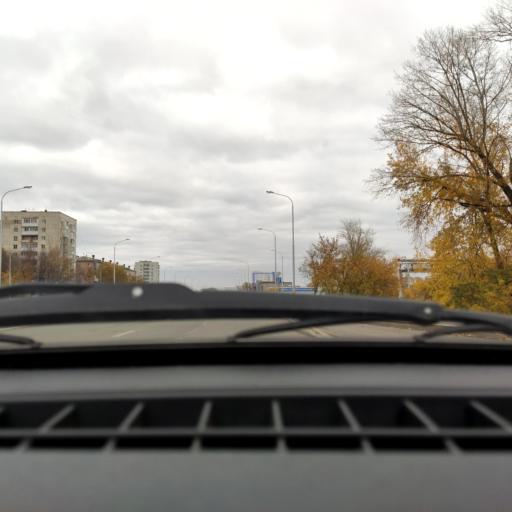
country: RU
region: Bashkortostan
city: Ufa
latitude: 54.8000
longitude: 56.1185
